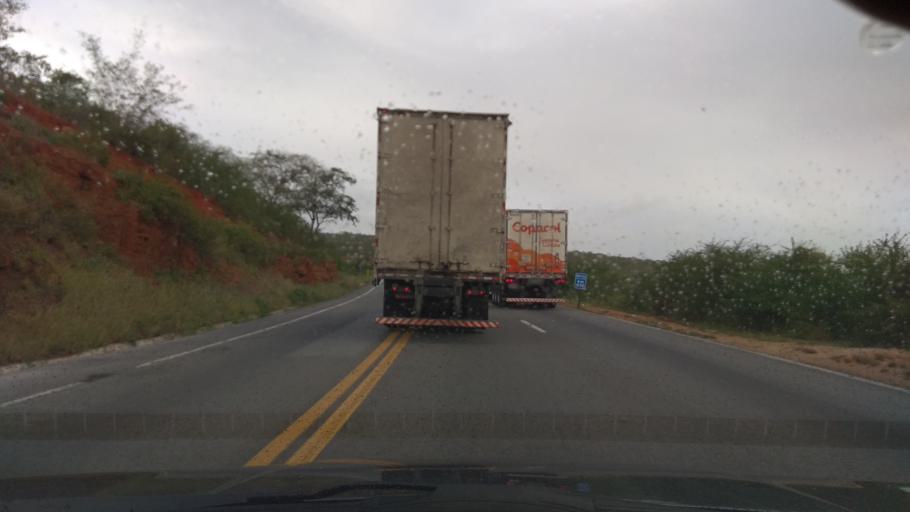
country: BR
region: Bahia
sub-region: Santa Ines
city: Santa Ines
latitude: -13.0396
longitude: -39.9681
